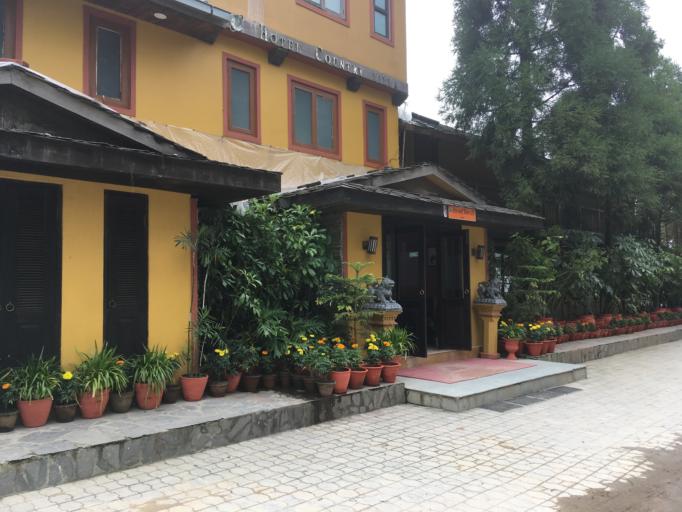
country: NP
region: Central Region
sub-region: Bagmati Zone
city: Nagarkot
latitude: 27.7266
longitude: 85.5251
